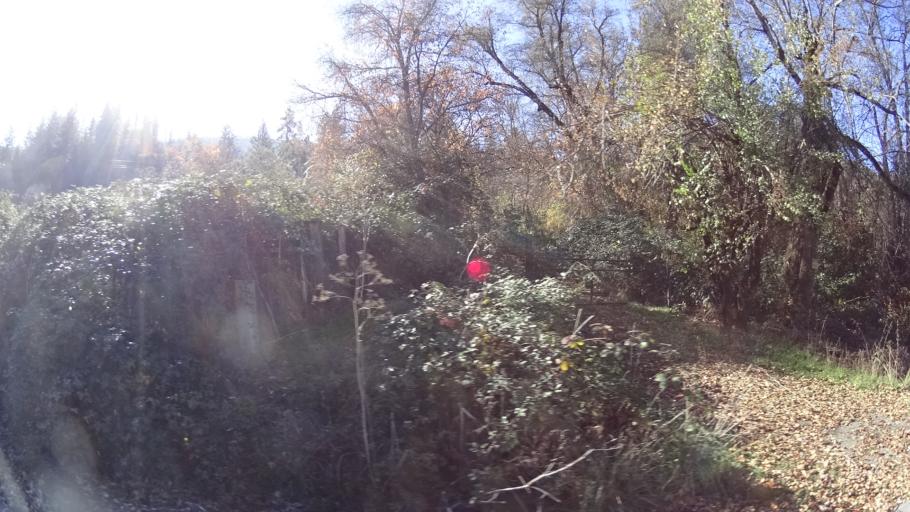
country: US
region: California
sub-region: Siskiyou County
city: Yreka
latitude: 41.8222
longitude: -122.9655
